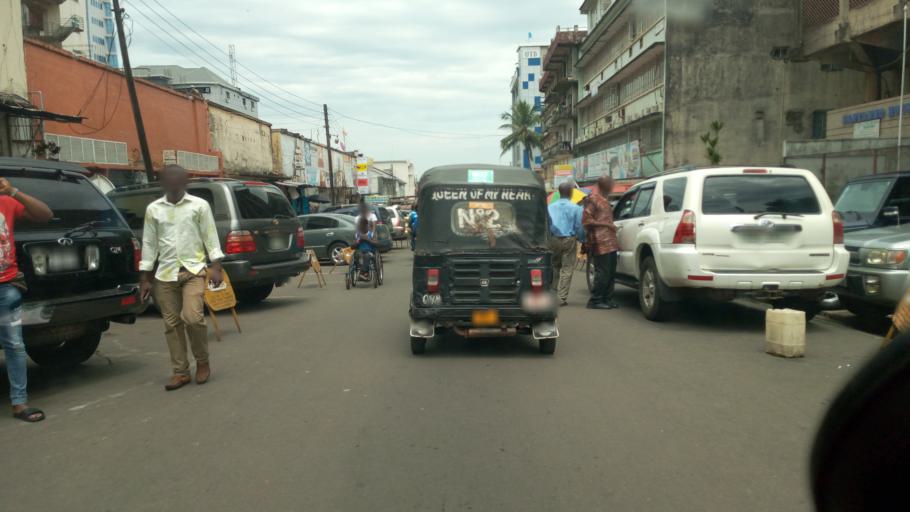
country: SL
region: Western Area
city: Freetown
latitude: 8.4896
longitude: -13.2335
